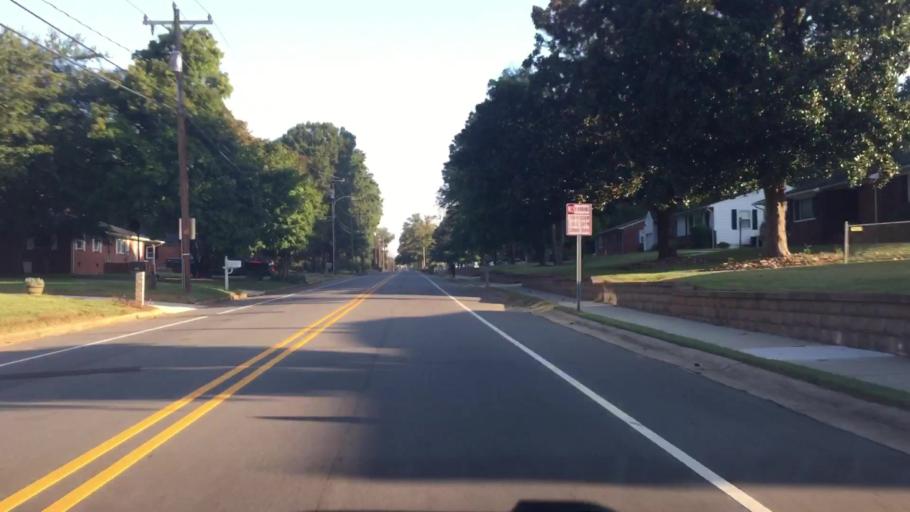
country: US
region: North Carolina
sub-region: Iredell County
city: Mooresville
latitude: 35.5718
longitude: -80.8014
